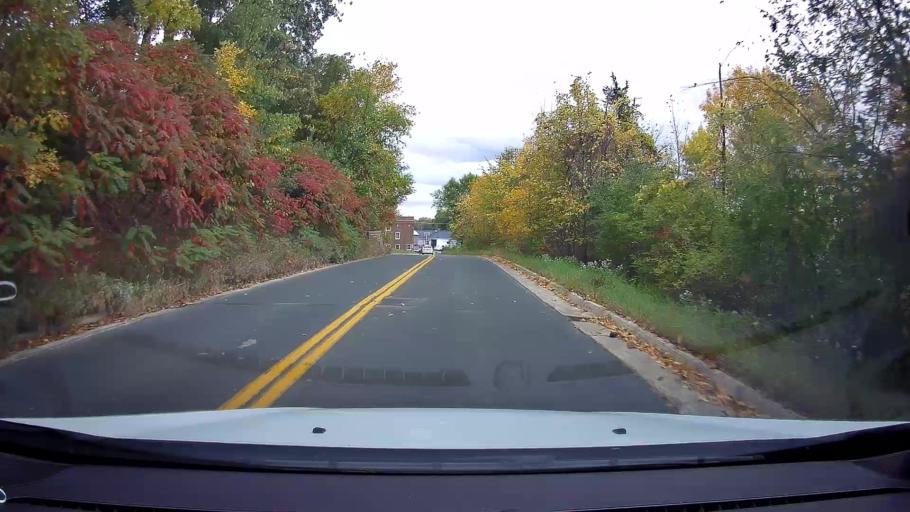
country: US
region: Minnesota
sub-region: Chisago County
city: Center City
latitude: 45.3934
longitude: -92.8171
